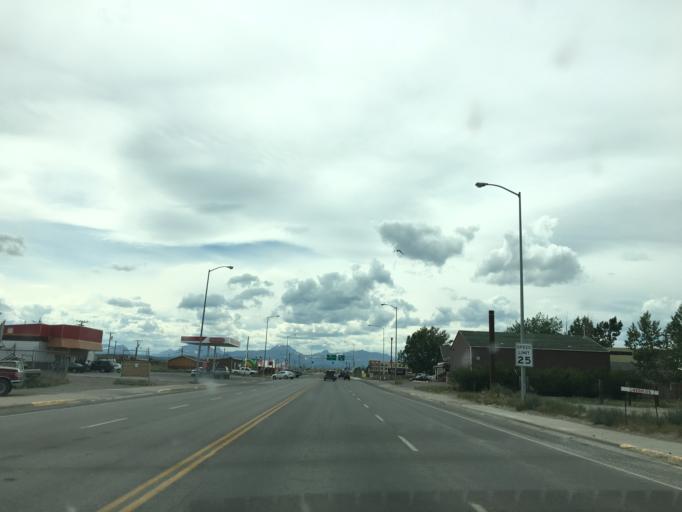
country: US
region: Montana
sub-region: Glacier County
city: Browning
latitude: 48.5560
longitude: -113.0187
